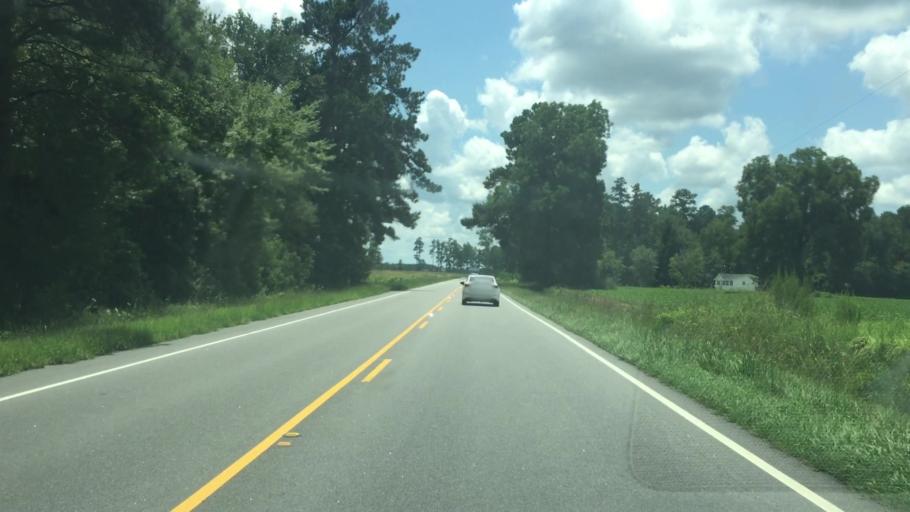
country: US
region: North Carolina
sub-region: Columbus County
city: Tabor City
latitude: 34.1822
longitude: -78.8390
